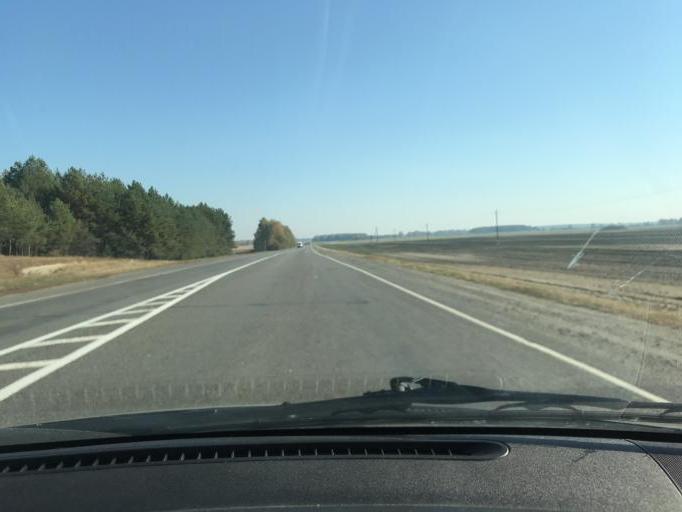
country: BY
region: Brest
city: Davyd-Haradok
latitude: 52.2437
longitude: 27.1600
